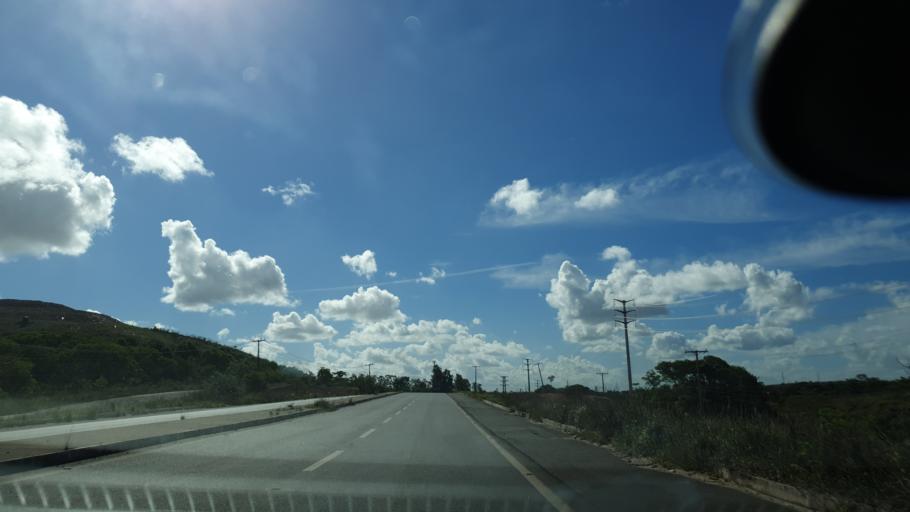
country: BR
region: Bahia
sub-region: Camacari
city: Camacari
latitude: -12.6852
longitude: -38.2568
